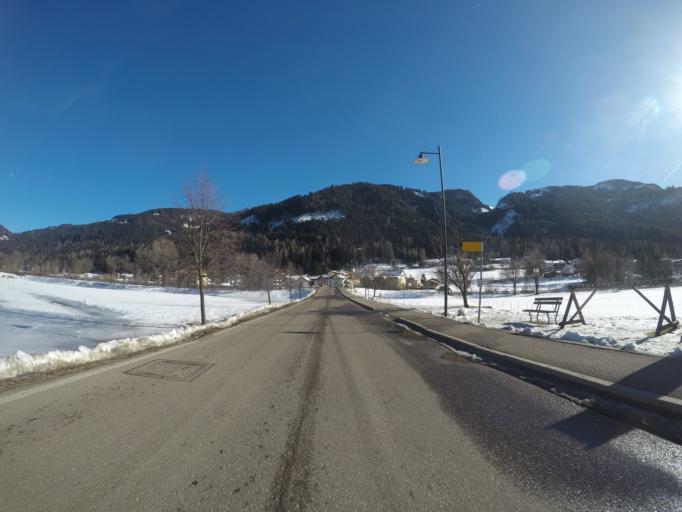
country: IT
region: Trentino-Alto Adige
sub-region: Provincia di Trento
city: Ziano di Fiemme
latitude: 46.2878
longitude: 11.5700
